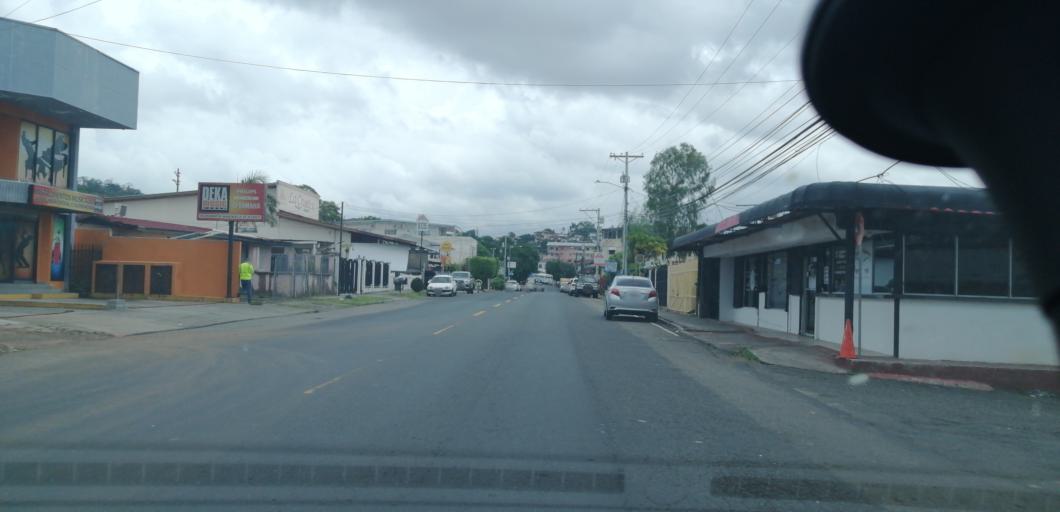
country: PA
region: Panama
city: Panama
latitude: 9.0082
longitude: -79.5230
